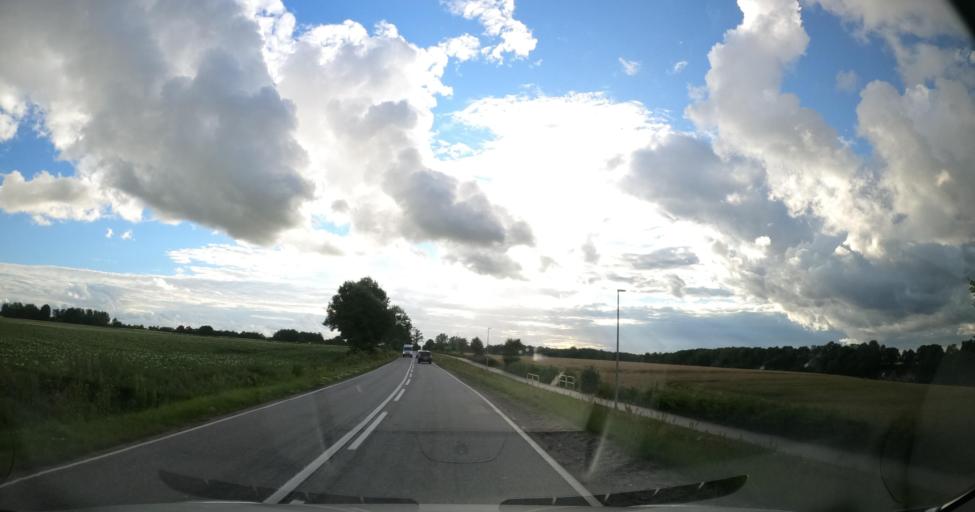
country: PL
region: Pomeranian Voivodeship
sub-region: Powiat slupski
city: Potegowo
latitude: 54.4176
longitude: 17.4059
